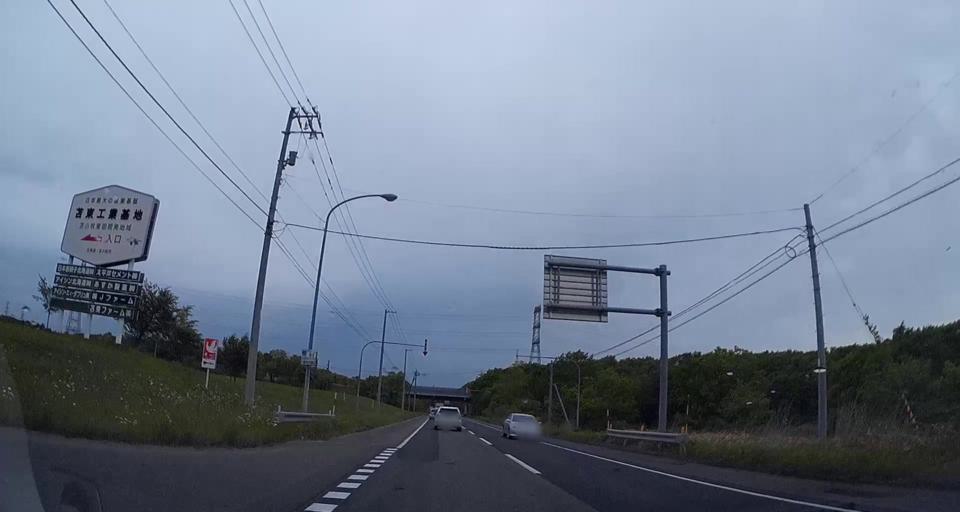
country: JP
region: Hokkaido
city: Chitose
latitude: 42.7111
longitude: 141.7486
